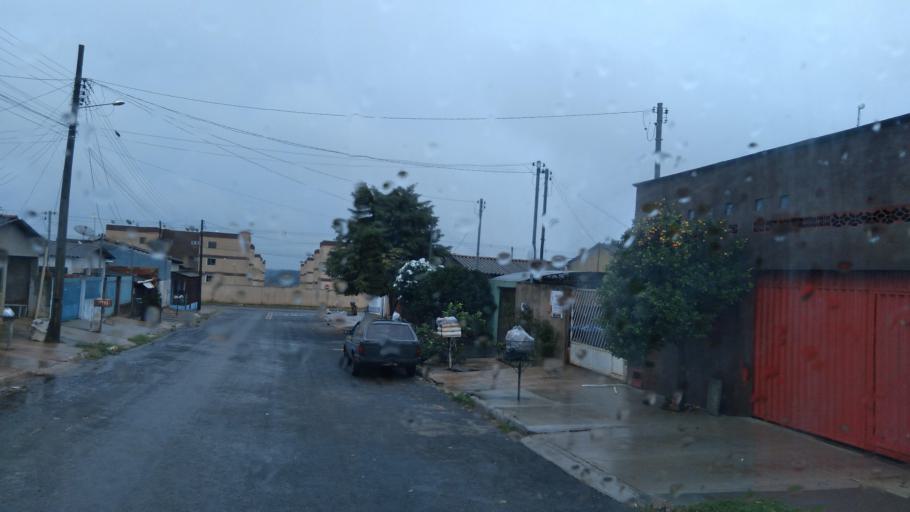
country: BR
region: Goias
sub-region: Mineiros
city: Mineiros
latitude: -17.5397
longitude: -52.5421
